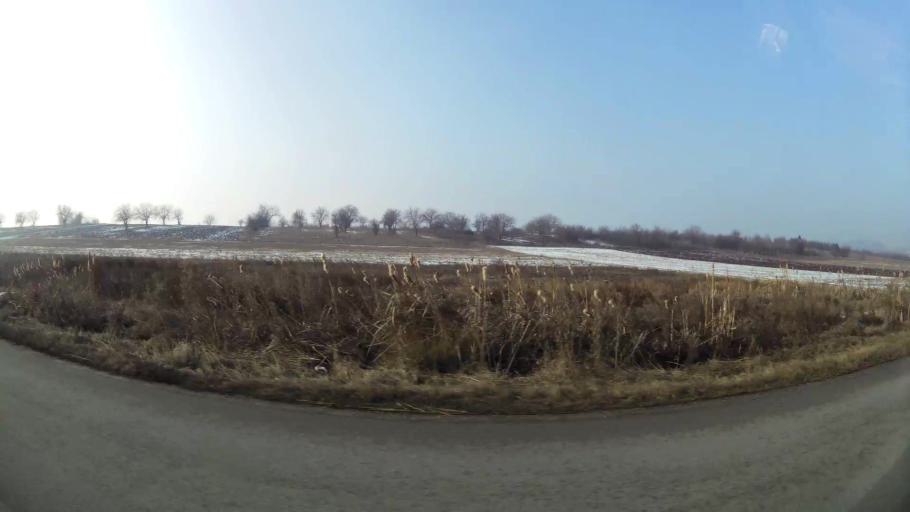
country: MK
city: Kadino
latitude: 41.9751
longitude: 21.6094
